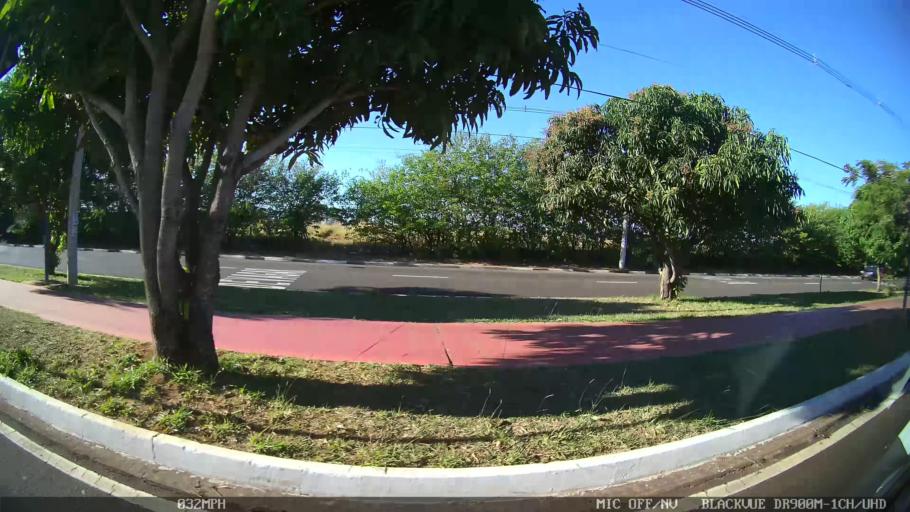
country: BR
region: Sao Paulo
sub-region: Franca
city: Franca
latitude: -20.5713
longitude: -47.3684
